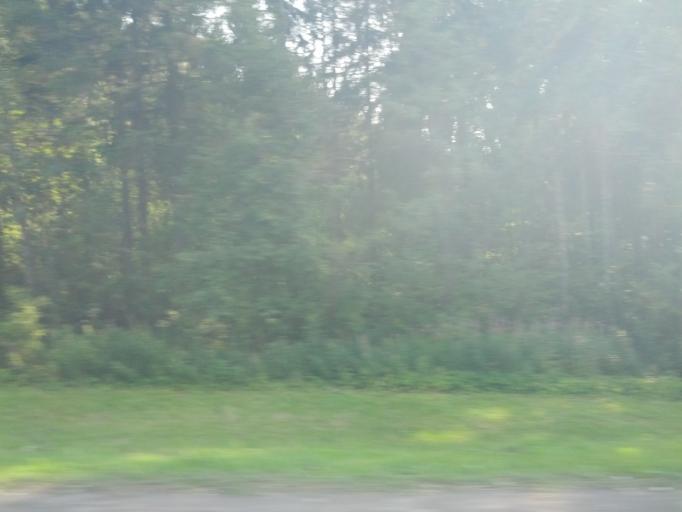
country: RU
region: Leningrad
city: Yanino Vtoroye
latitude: 59.8897
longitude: 30.5766
